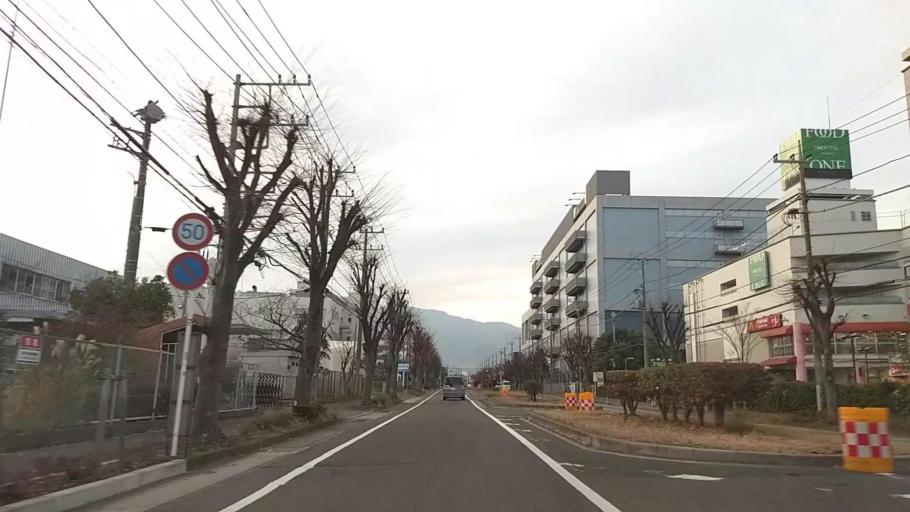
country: JP
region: Kanagawa
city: Atsugi
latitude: 35.4275
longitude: 139.3437
